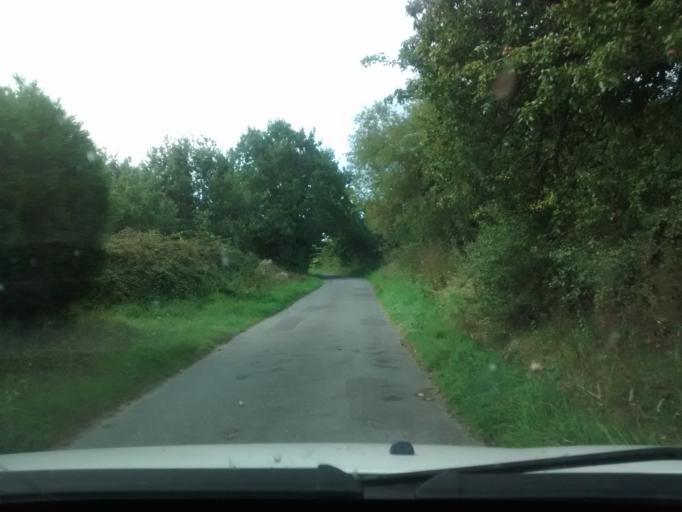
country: FR
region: Brittany
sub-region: Departement d'Ille-et-Vilaine
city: Saint-Lunaire
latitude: 48.6280
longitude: -2.1112
